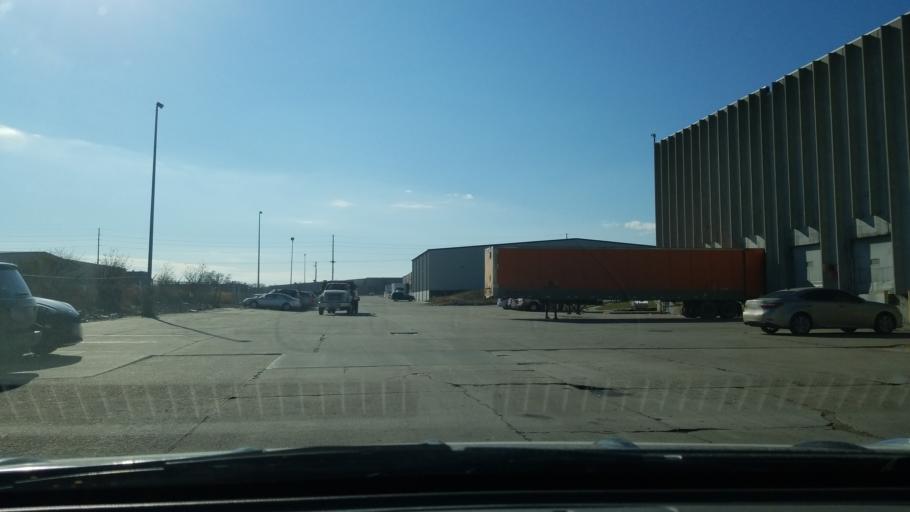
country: US
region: Nebraska
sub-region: Douglas County
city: Ralston
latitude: 41.2184
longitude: -96.0737
